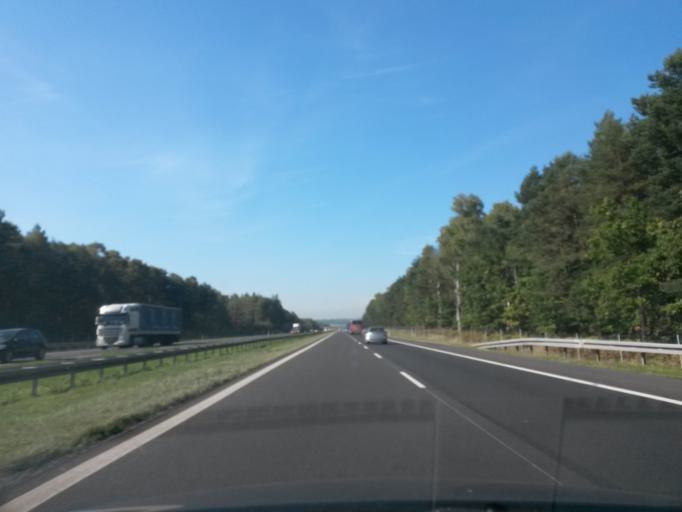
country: PL
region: Lesser Poland Voivodeship
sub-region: Powiat chrzanowski
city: Trzebinia
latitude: 50.1402
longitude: 19.4576
